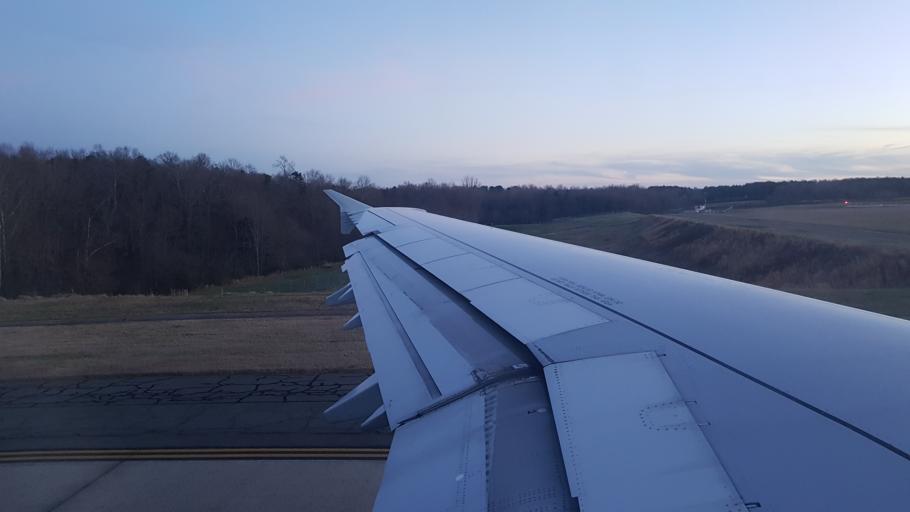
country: US
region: North Carolina
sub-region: Gaston County
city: Belmont
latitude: 35.2002
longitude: -80.9493
